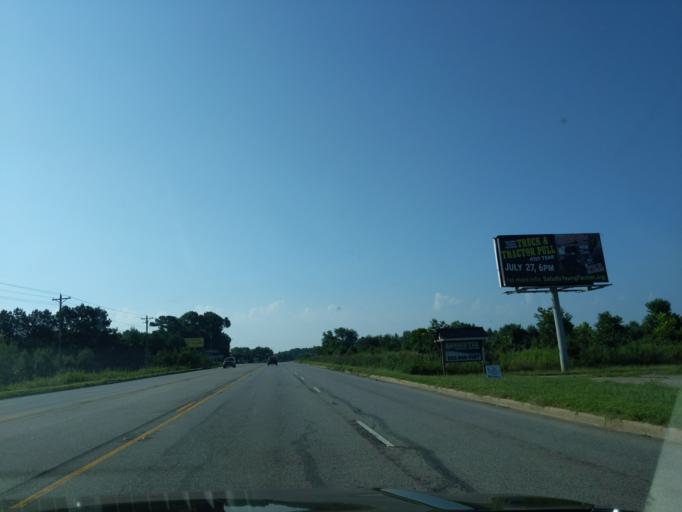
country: US
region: South Carolina
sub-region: Newberry County
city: Newberry
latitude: 34.2537
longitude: -81.5755
